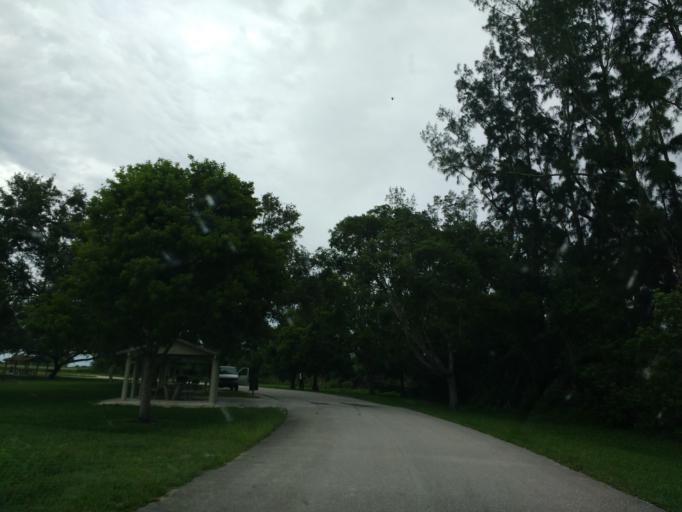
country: US
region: Florida
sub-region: Palm Beach County
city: South Bay
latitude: 26.6978
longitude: -80.8136
